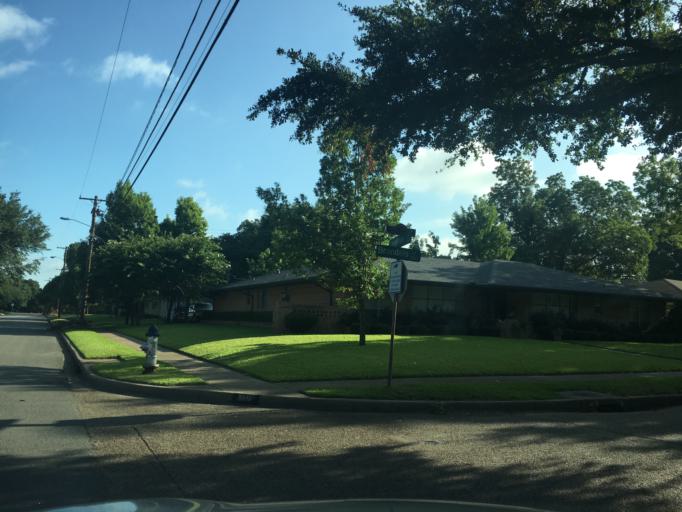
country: US
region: Texas
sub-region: Dallas County
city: Highland Park
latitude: 32.8447
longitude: -96.7607
